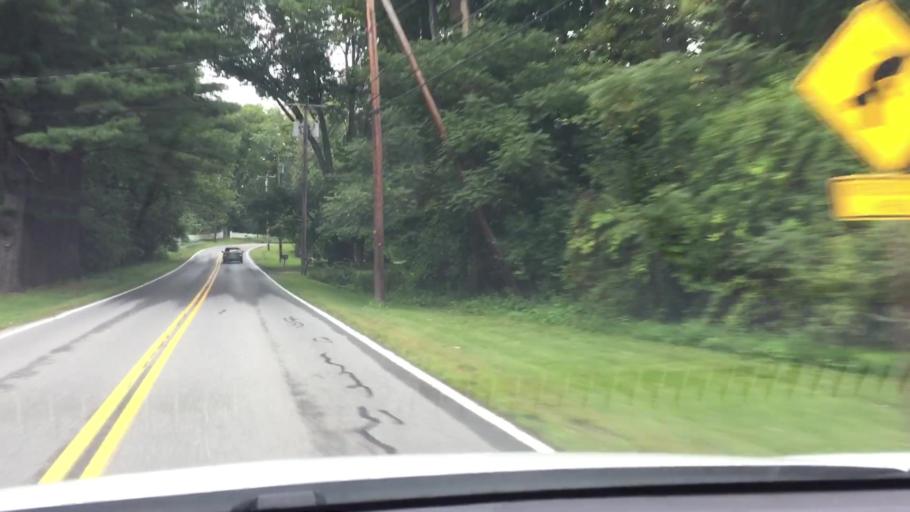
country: US
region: Massachusetts
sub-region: Berkshire County
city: Housatonic
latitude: 42.2633
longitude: -73.3801
